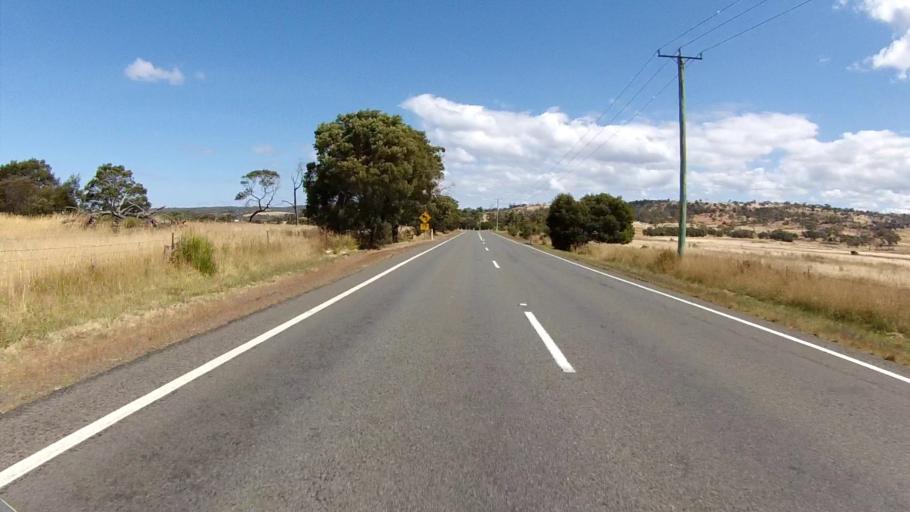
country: AU
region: Tasmania
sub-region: Break O'Day
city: St Helens
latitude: -42.1041
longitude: 148.0589
